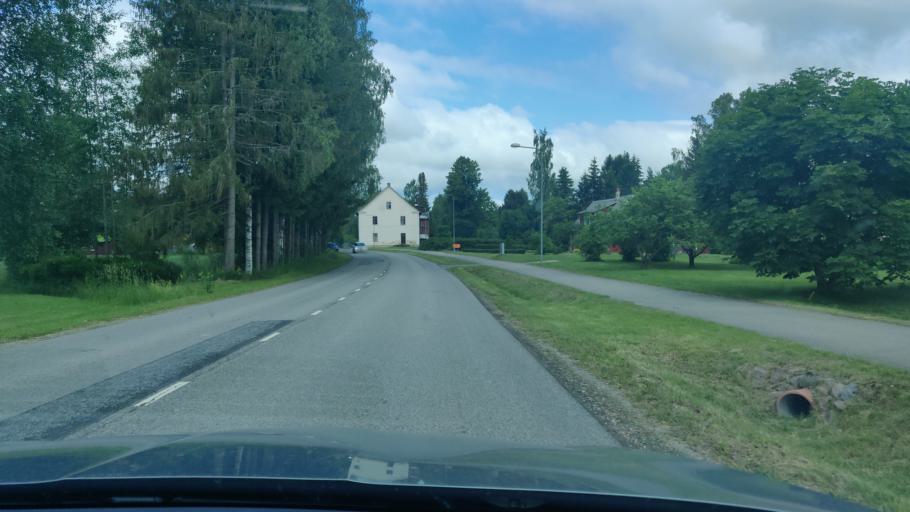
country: EE
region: Vorumaa
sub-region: Voru linn
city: Voru
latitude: 57.7290
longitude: 27.2949
